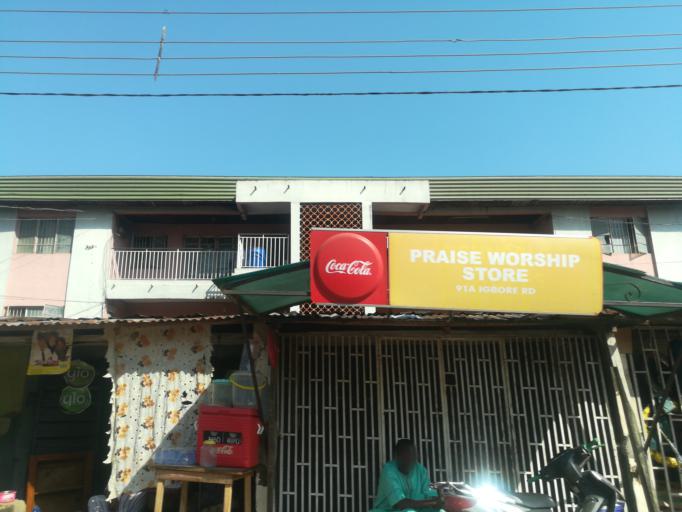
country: NG
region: Ogun
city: Abeokuta
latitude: 7.1481
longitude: 3.3391
